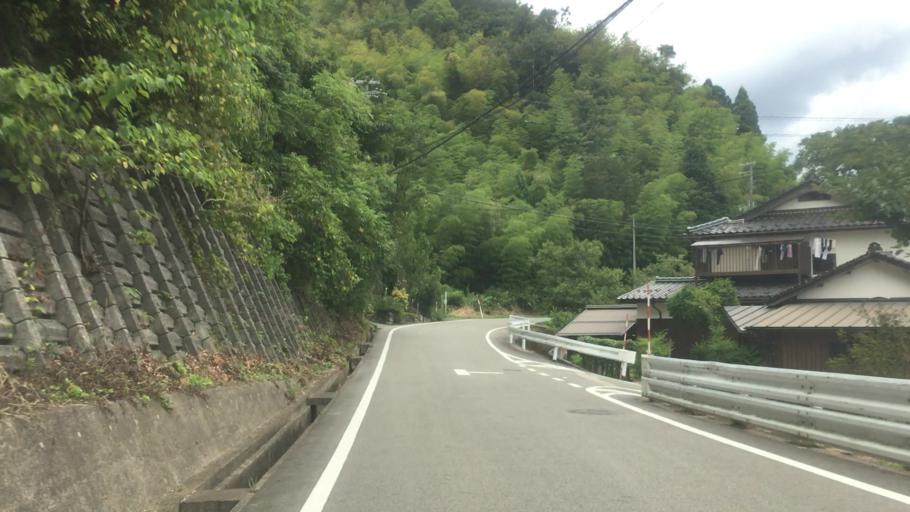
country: JP
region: Hyogo
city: Toyooka
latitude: 35.5973
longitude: 134.8009
